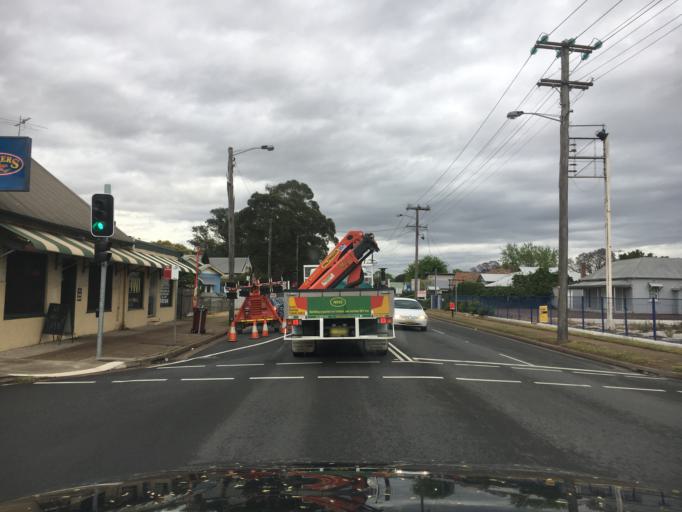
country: AU
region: New South Wales
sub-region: Singleton
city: Singleton
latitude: -32.5683
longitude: 151.1795
